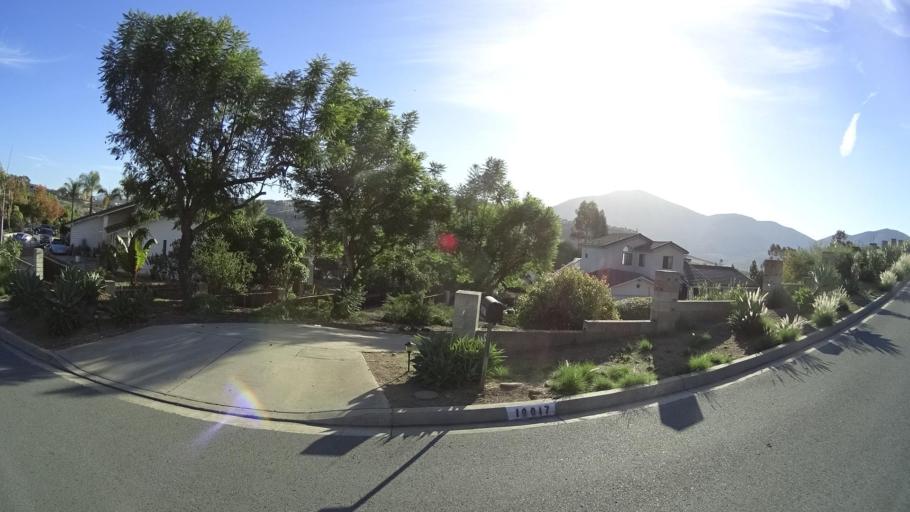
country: US
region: California
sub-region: San Diego County
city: La Presa
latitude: 32.7177
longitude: -116.9804
